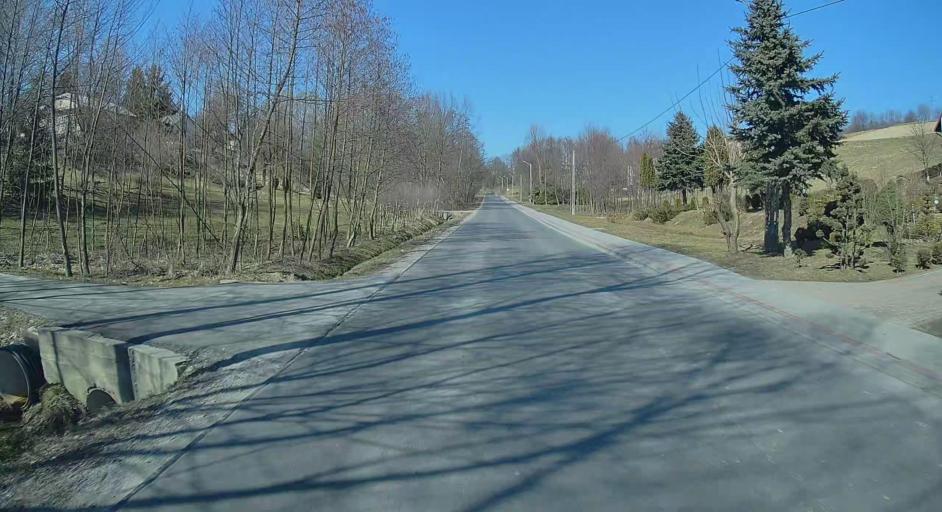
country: PL
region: Subcarpathian Voivodeship
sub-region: Powiat rzeszowski
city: Hyzne
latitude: 49.8884
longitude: 22.2281
